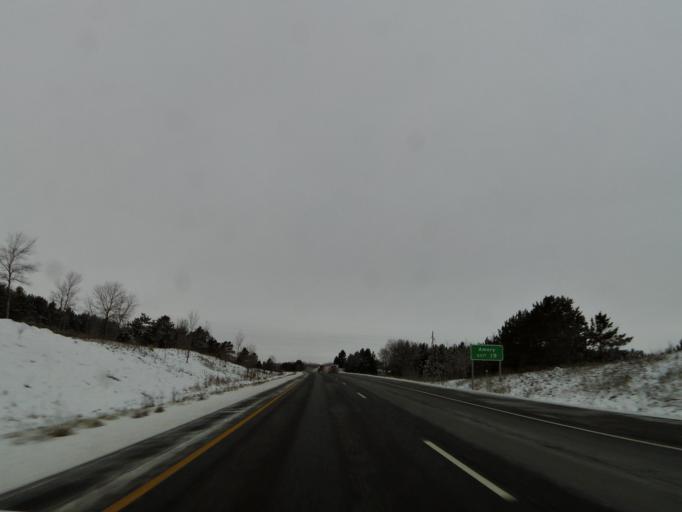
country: US
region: Wisconsin
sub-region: Saint Croix County
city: Baldwin
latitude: 44.9389
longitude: -92.3523
